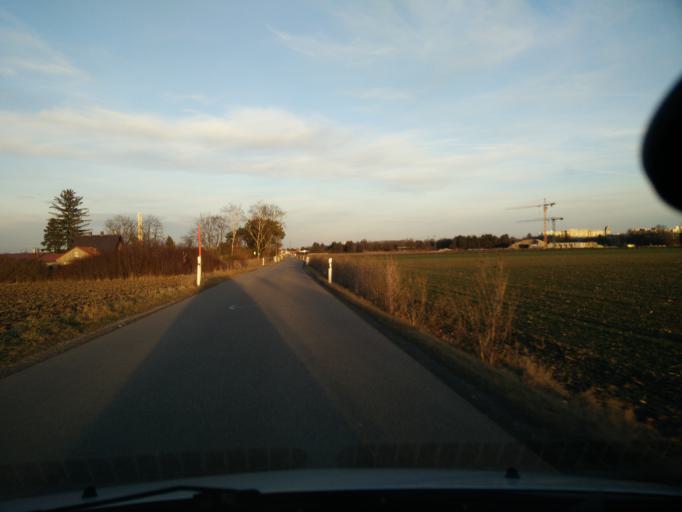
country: DE
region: Bavaria
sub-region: Upper Bavaria
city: Germering
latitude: 48.1519
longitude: 11.3998
